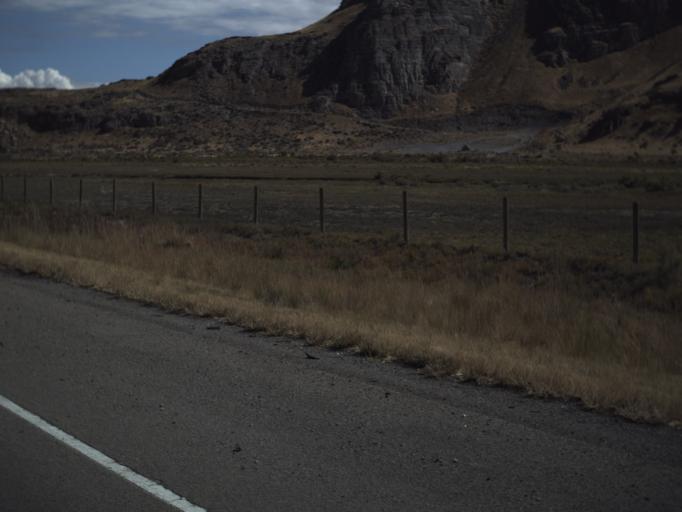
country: US
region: Utah
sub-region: Tooele County
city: Grantsville
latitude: 40.7450
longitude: -112.6468
